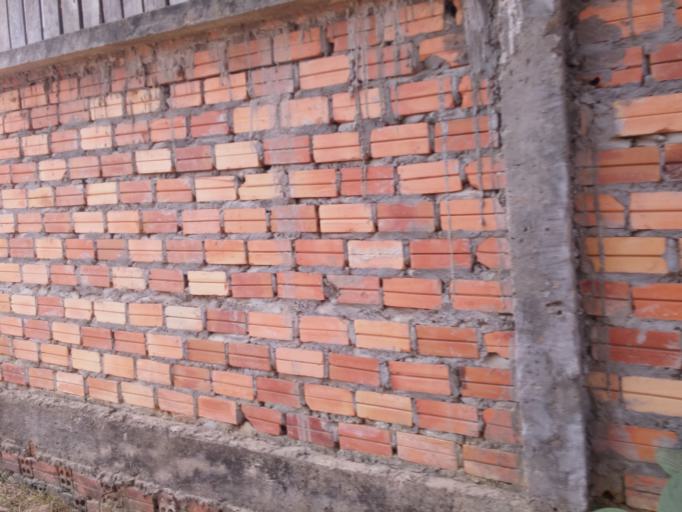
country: KH
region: Siem Reap
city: Siem Reap
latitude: 13.3586
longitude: 103.8907
